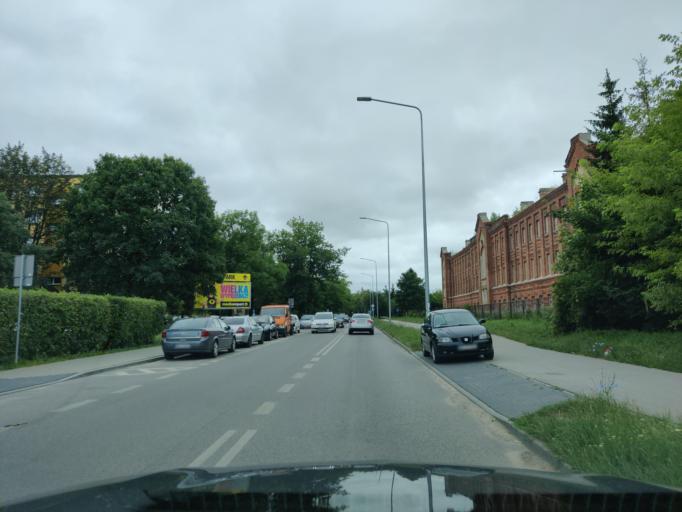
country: PL
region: Masovian Voivodeship
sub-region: Powiat pultuski
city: Pultusk
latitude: 52.7084
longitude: 21.0782
